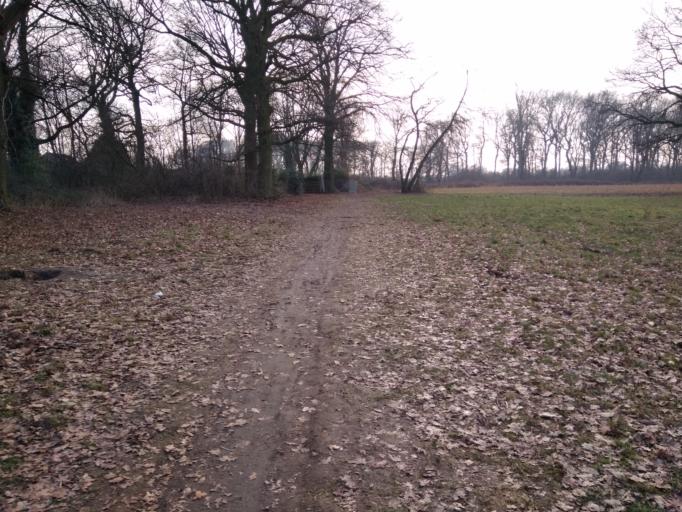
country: DE
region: North Rhine-Westphalia
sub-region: Regierungsbezirk Munster
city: Gladbeck
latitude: 51.5876
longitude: 7.0131
